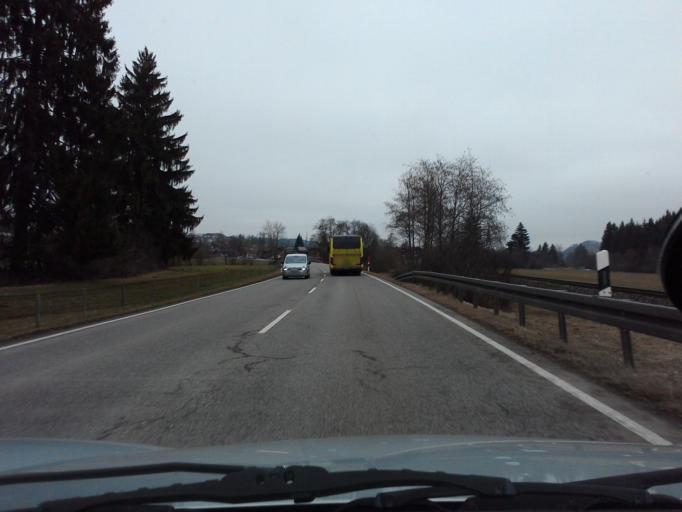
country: DE
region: Bavaria
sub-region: Swabia
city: Obermaiselstein
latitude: 47.4521
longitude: 10.2723
